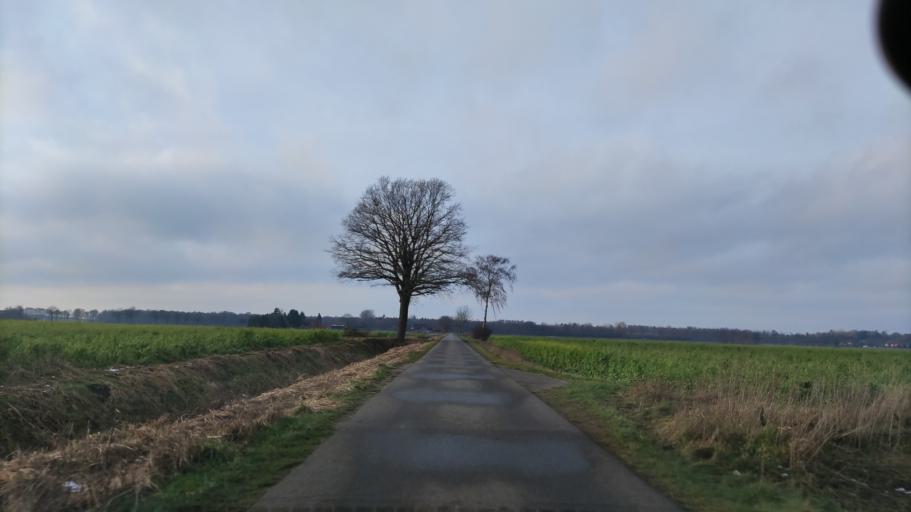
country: DE
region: Lower Saxony
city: Ludersburg
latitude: 53.3068
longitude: 10.5830
